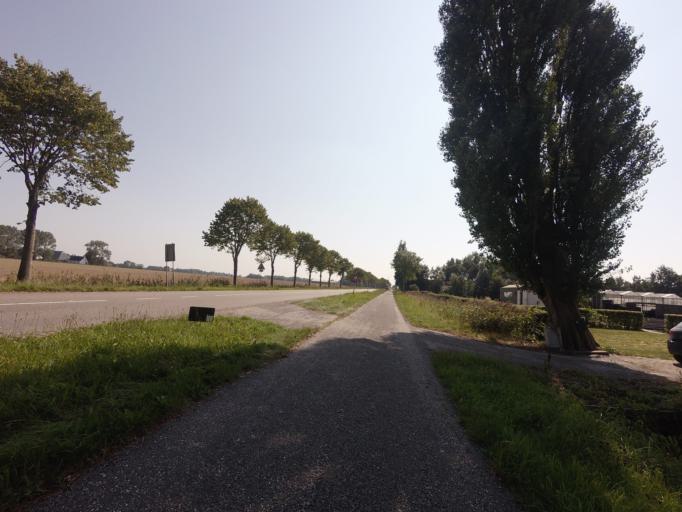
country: NL
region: Groningen
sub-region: Gemeente Zuidhorn
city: Grijpskerk
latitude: 53.2941
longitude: 6.2963
